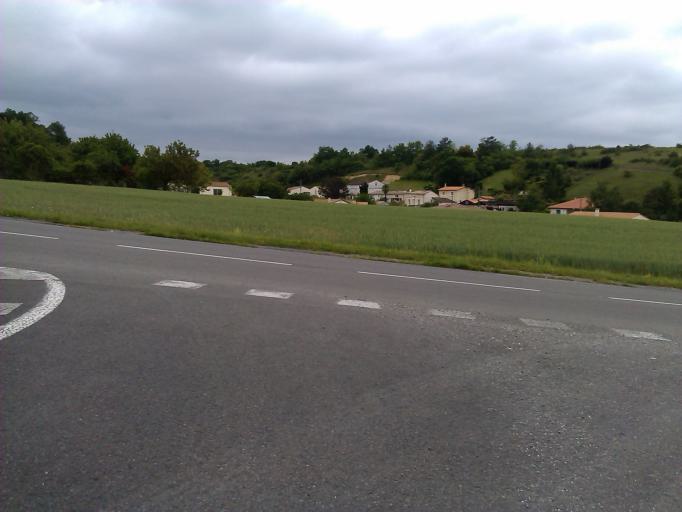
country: FR
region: Poitou-Charentes
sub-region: Departement de la Charente
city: Chateauneuf-sur-Charente
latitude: 45.5904
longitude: -0.0516
